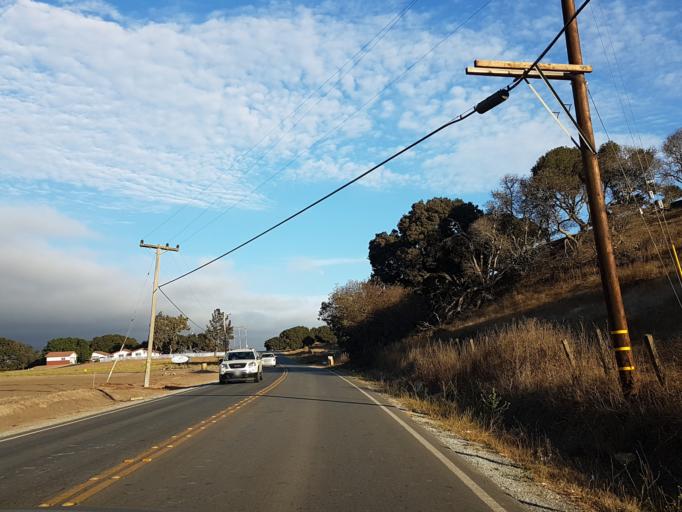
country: US
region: California
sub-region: Monterey County
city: Chualar
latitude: 36.5745
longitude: -121.5839
